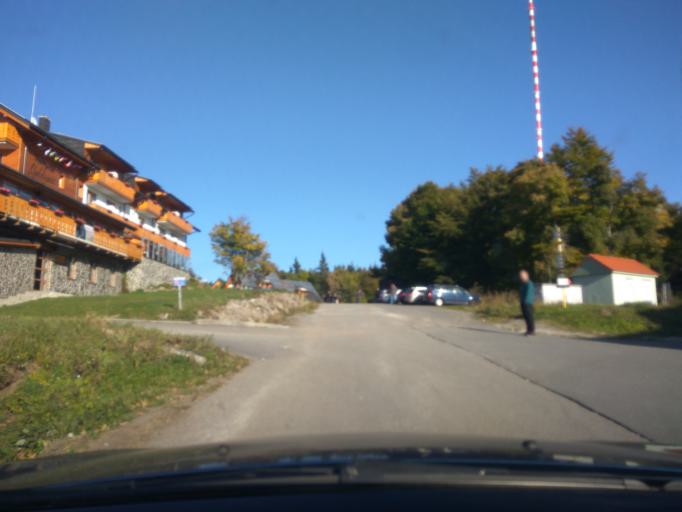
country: SK
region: Banskobystricky
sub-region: Okres Ziar nad Hronom
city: Kremnica
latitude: 48.7398
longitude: 18.9902
